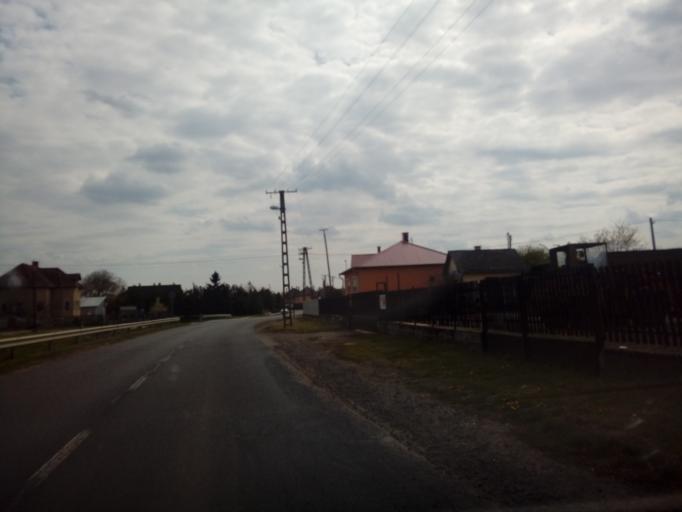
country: HU
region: Szabolcs-Szatmar-Bereg
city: Balkany
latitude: 47.8155
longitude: 21.8510
